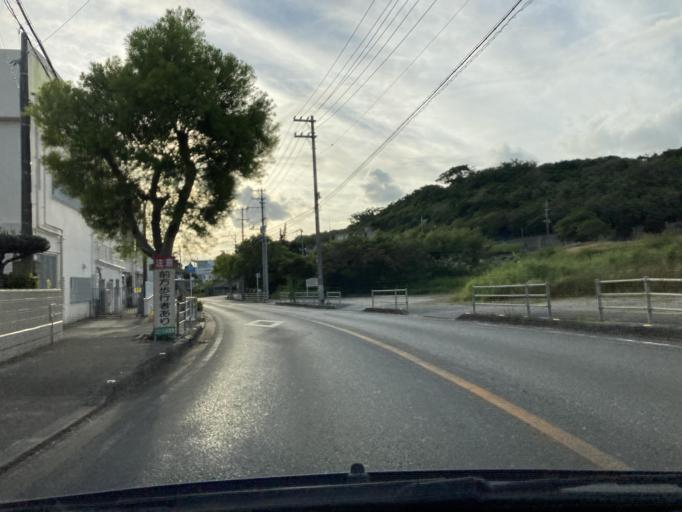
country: JP
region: Okinawa
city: Tomigusuku
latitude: 26.1517
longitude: 127.7038
